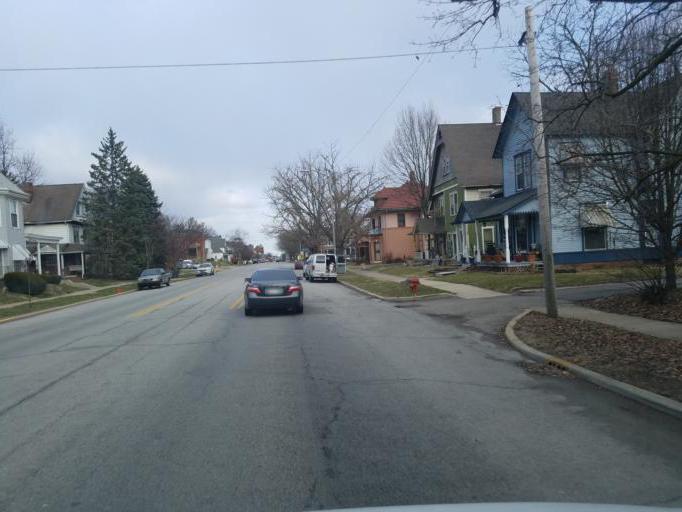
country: US
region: Indiana
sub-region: Hancock County
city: Greenfield
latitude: 39.7848
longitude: -85.7764
